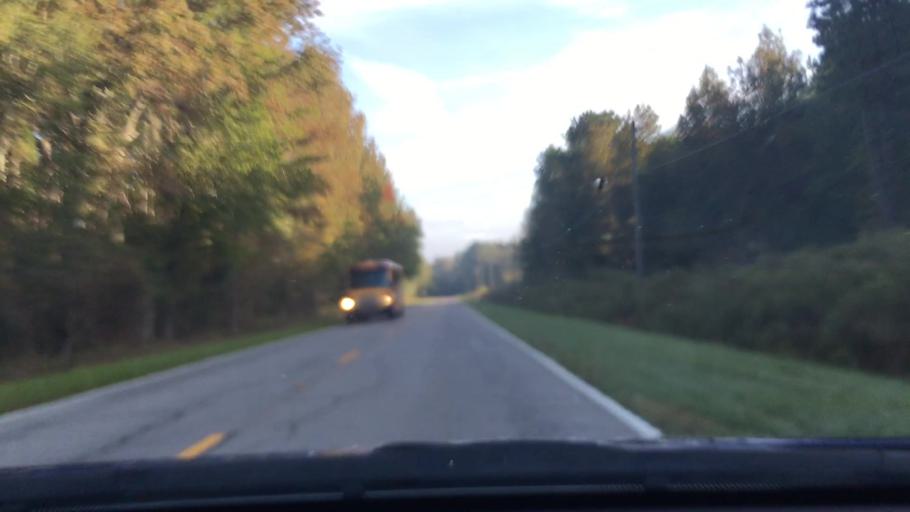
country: US
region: South Carolina
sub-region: Sumter County
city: East Sumter
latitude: 33.9579
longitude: -80.3051
